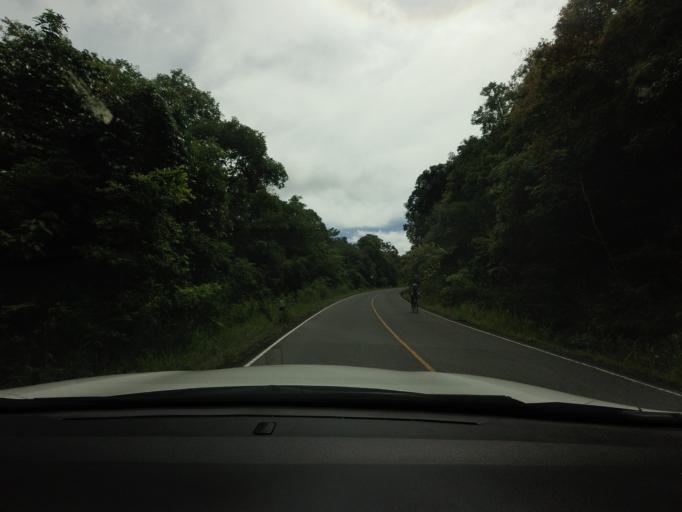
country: TH
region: Nakhon Nayok
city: Nakhon Nayok
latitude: 14.3880
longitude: 101.3527
